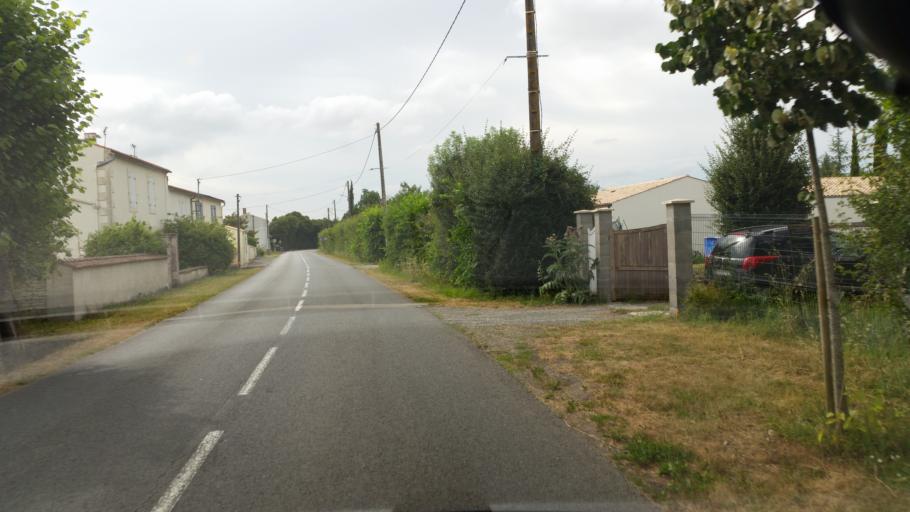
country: FR
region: Poitou-Charentes
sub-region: Departement de la Charente-Maritime
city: Saint-Jean-de-Liversay
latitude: 46.2134
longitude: -0.8788
